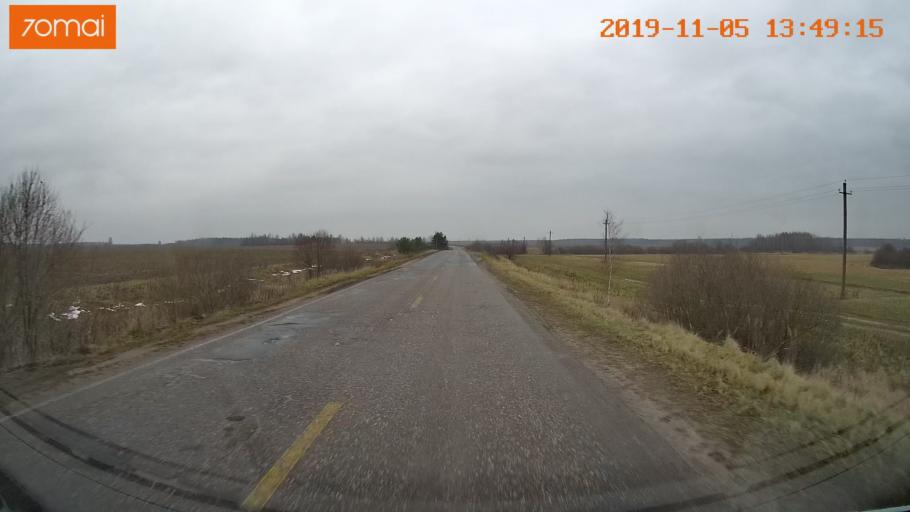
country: RU
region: Ivanovo
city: Kaminskiy
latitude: 57.0088
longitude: 41.4088
